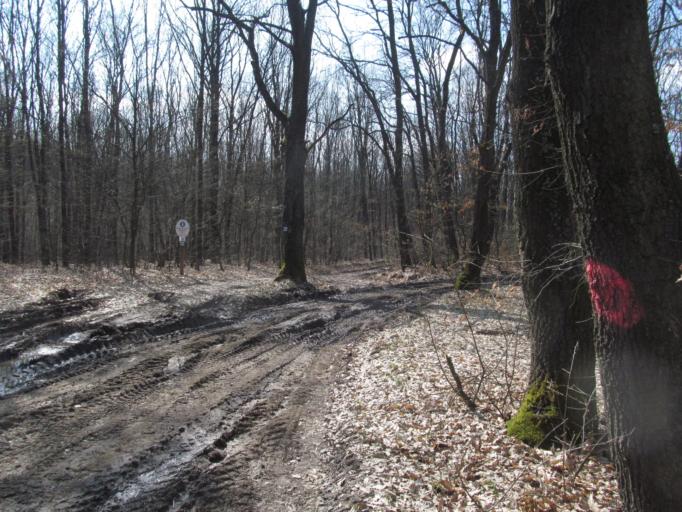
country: HU
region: Borsod-Abauj-Zemplen
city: Putnok
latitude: 48.3443
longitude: 20.4343
